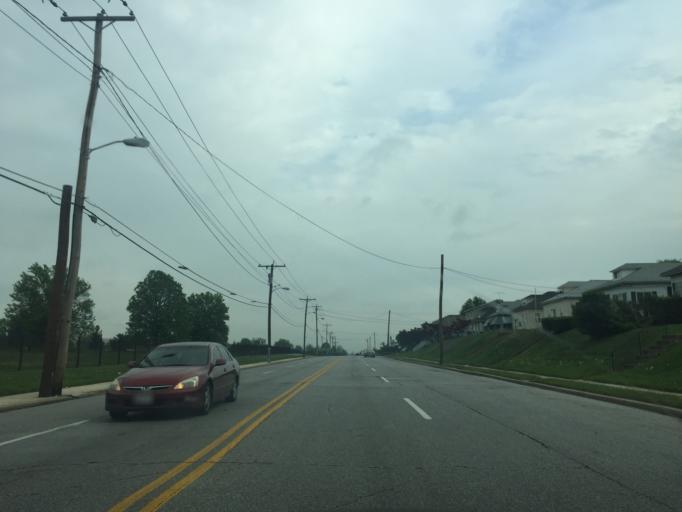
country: US
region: Maryland
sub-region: Baltimore County
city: Charlestown
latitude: 39.2689
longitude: -76.6865
